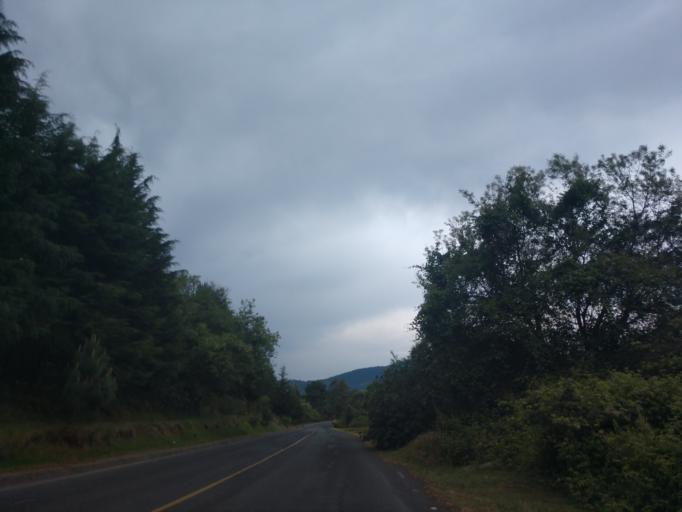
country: MX
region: Jalisco
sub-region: Mazamitla
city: Mazamitla
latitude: 19.9215
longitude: -103.0365
